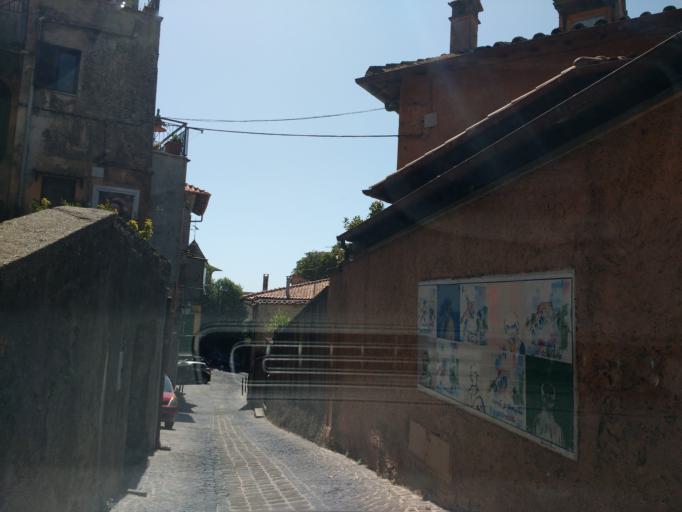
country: IT
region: Latium
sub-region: Citta metropolitana di Roma Capitale
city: Rocca di Papa
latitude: 41.7619
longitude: 12.7088
